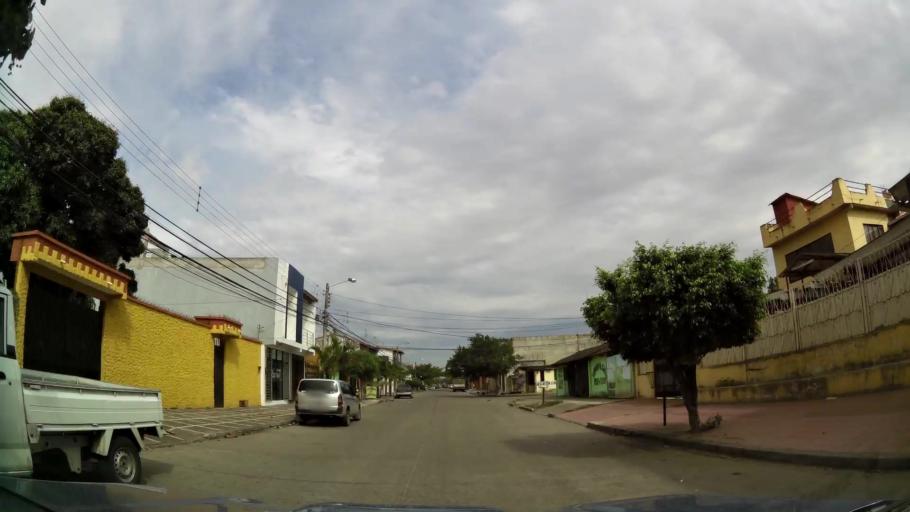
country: BO
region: Santa Cruz
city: Santa Cruz de la Sierra
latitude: -17.7893
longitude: -63.1998
